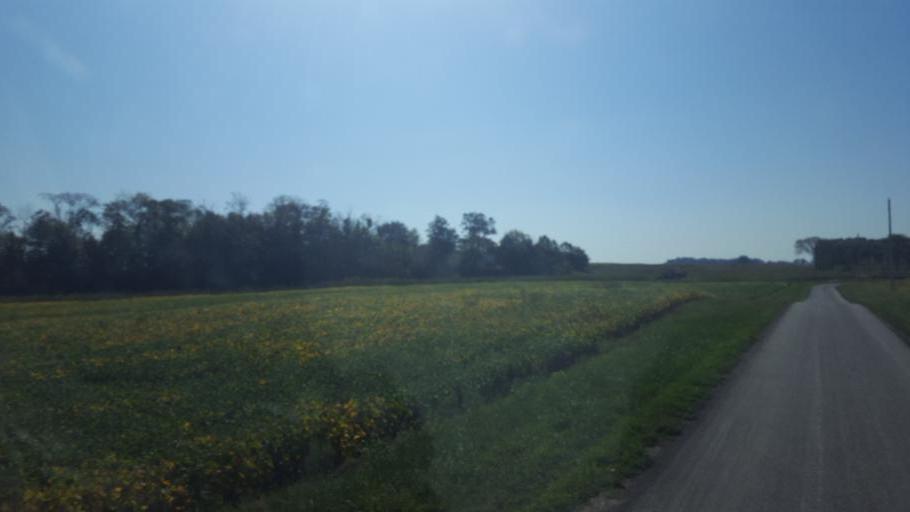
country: US
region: Ohio
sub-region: Union County
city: Richwood
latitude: 40.5547
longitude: -83.4337
